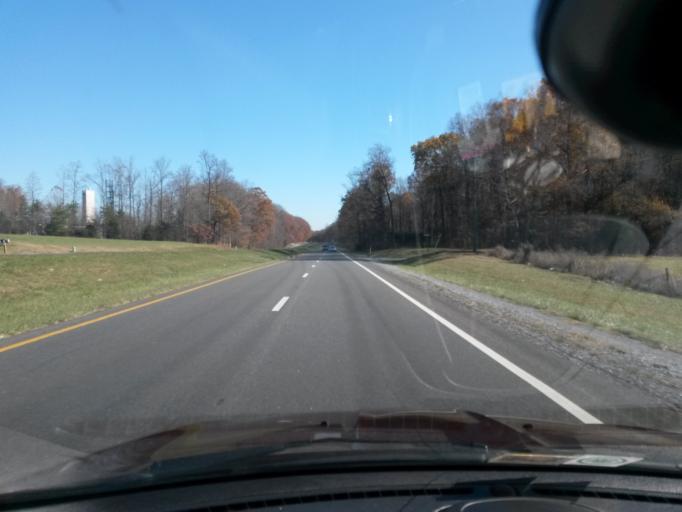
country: US
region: Virginia
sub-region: Bedford County
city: Forest
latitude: 37.3009
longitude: -79.3432
